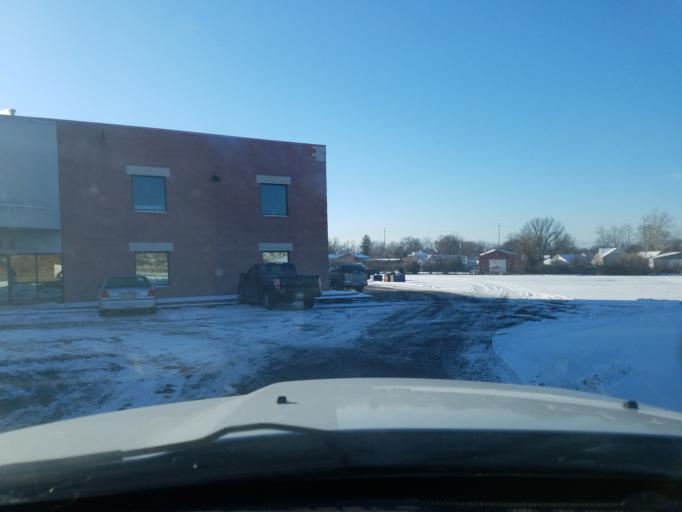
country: US
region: Indiana
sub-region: Marion County
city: Beech Grove
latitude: 39.7274
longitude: -86.0837
